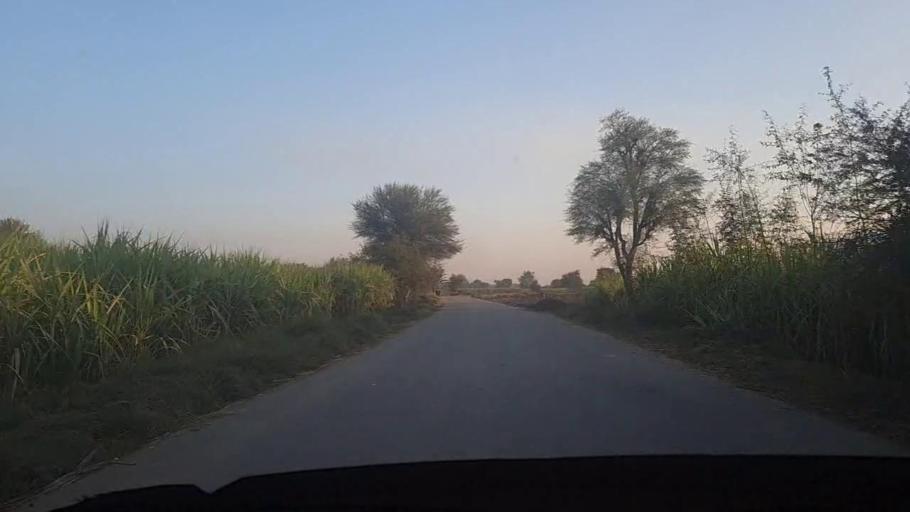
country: PK
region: Sindh
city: Sobhadero
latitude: 27.3507
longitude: 68.3753
